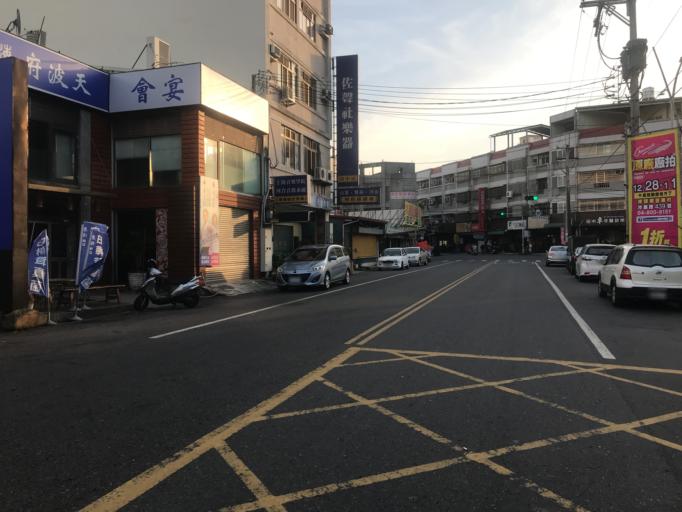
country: TW
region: Taiwan
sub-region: Nantou
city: Nantou
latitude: 23.8629
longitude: 120.5860
